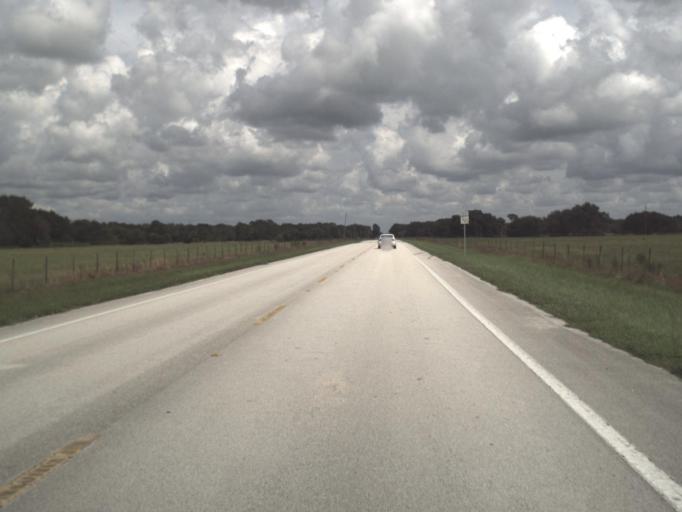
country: US
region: Florida
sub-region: Sarasota County
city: Warm Mineral Springs
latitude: 27.1934
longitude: -82.1643
